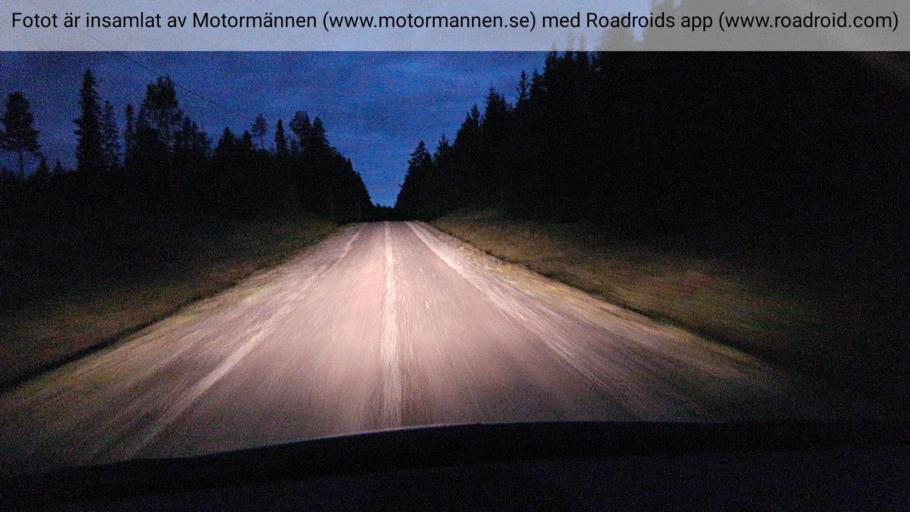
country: SE
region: Jaemtland
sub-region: OEstersunds Kommun
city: Lit
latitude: 63.3076
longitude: 15.2563
